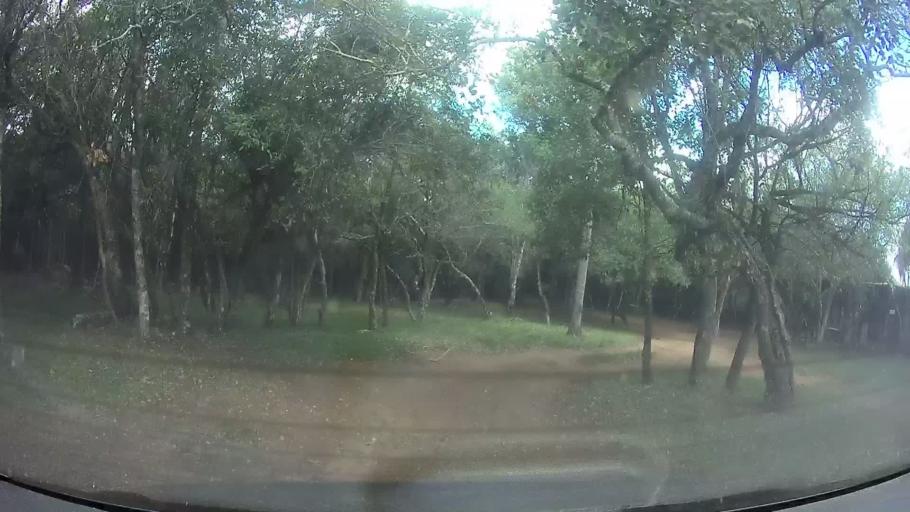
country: PY
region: Paraguari
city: La Colmena
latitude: -25.9732
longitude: -56.7281
